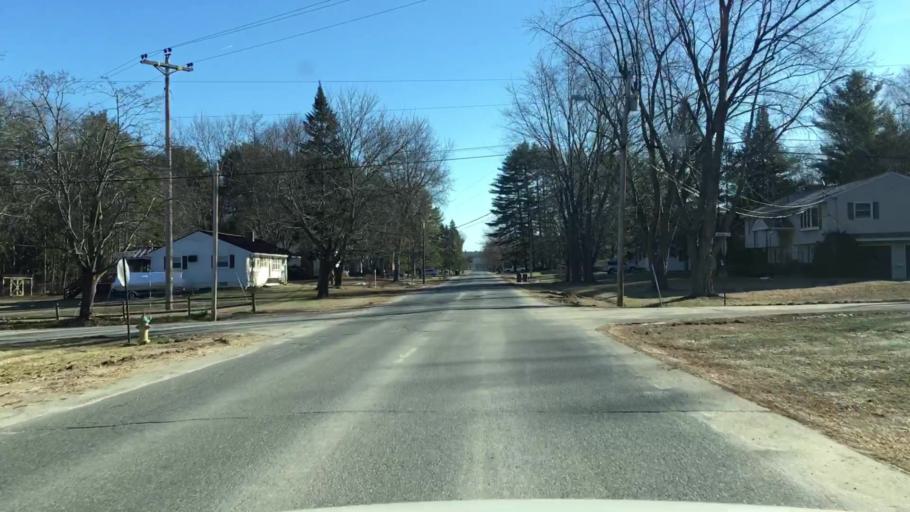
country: US
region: Maine
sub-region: Kennebec County
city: Winslow
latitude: 44.5492
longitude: -69.6049
